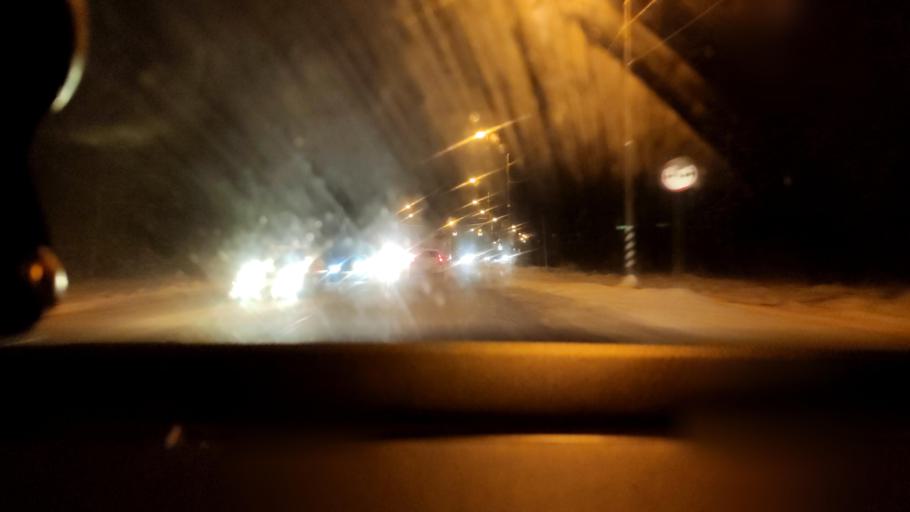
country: RU
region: Moskovskaya
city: Andreyevka
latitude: 55.9818
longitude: 37.0744
